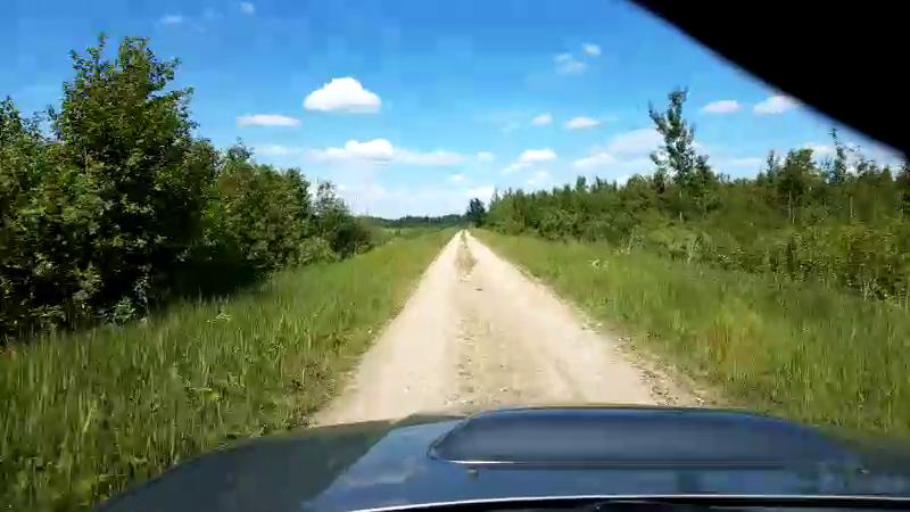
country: EE
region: Paernumaa
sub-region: Halinga vald
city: Parnu-Jaagupi
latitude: 58.5380
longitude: 24.5303
